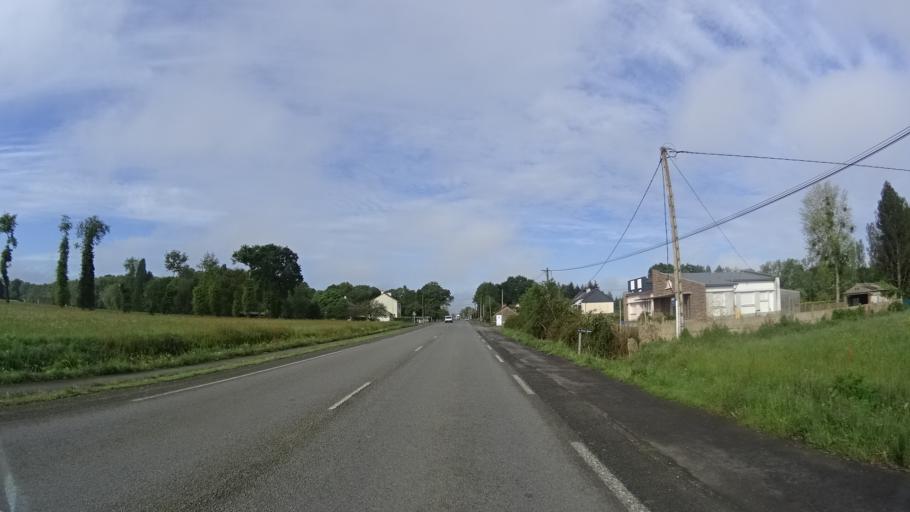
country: FR
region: Brittany
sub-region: Departement d'Ille-et-Vilaine
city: Mordelles
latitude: 48.0824
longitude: -1.8216
